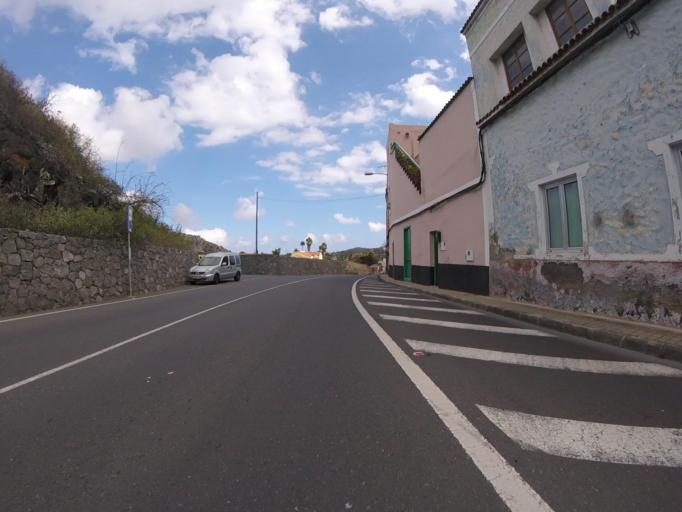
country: ES
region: Canary Islands
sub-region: Provincia de Las Palmas
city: Santa Brigida
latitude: 28.0578
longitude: -15.4728
